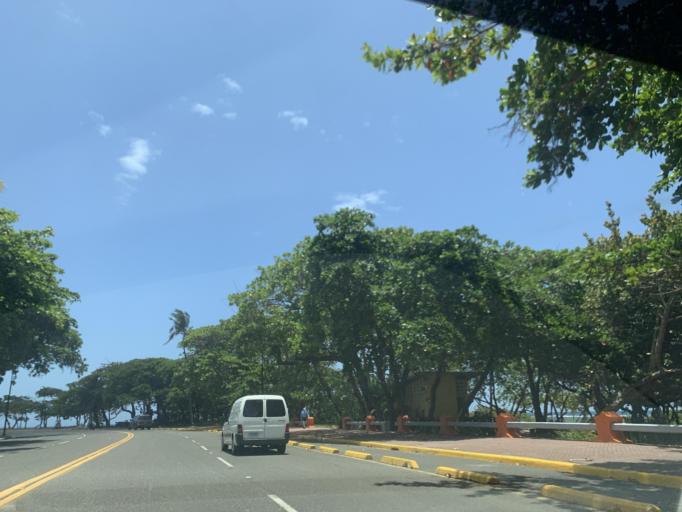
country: DO
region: Puerto Plata
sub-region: Puerto Plata
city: Puerto Plata
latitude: 19.7891
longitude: -70.6699
